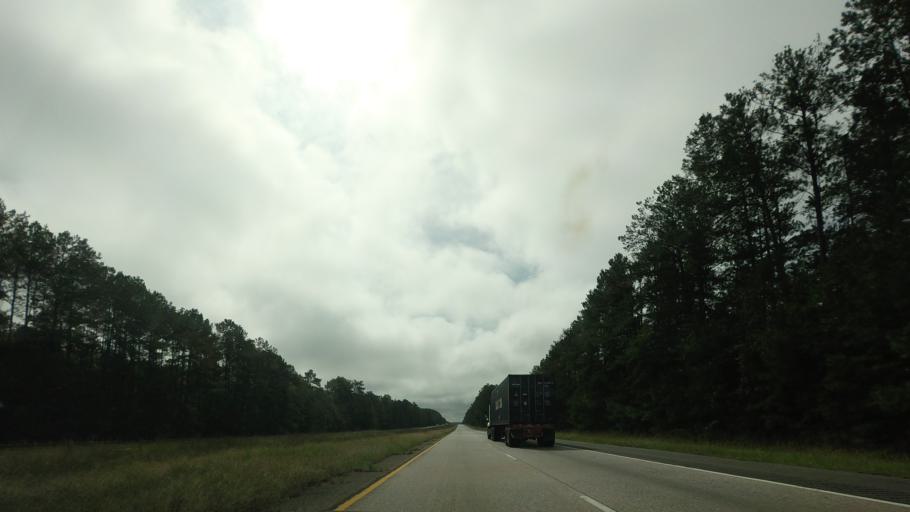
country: US
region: Georgia
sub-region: Bibb County
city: Macon
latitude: 32.7520
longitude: -83.5502
